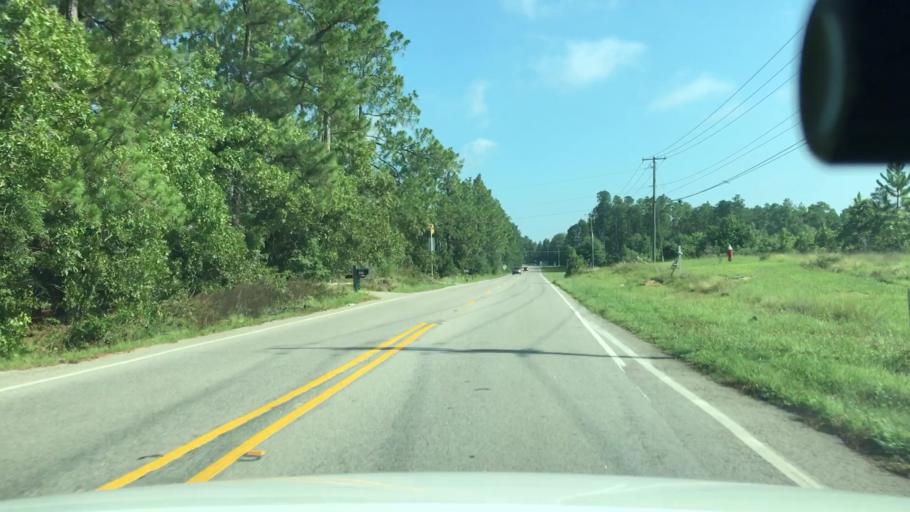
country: US
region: South Carolina
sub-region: Aiken County
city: Graniteville
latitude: 33.5867
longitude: -81.8363
